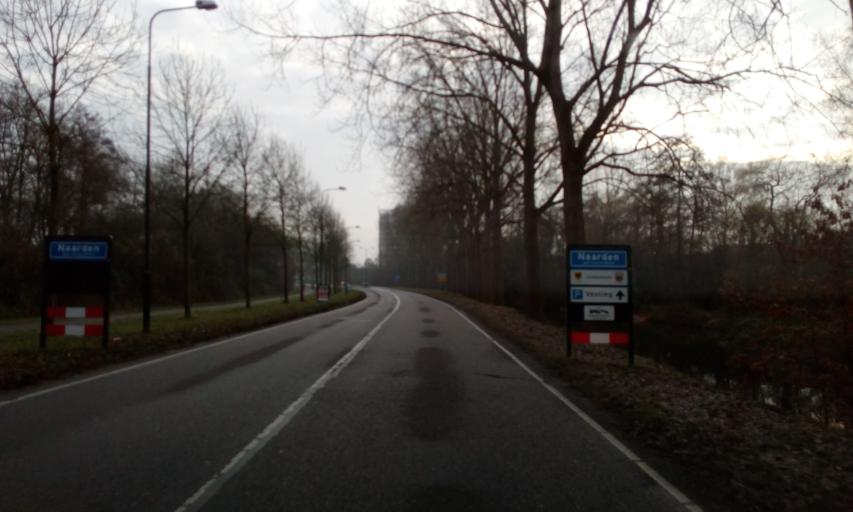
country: NL
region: North Holland
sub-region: Gemeente Naarden
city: Naarden
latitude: 52.2920
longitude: 5.1474
